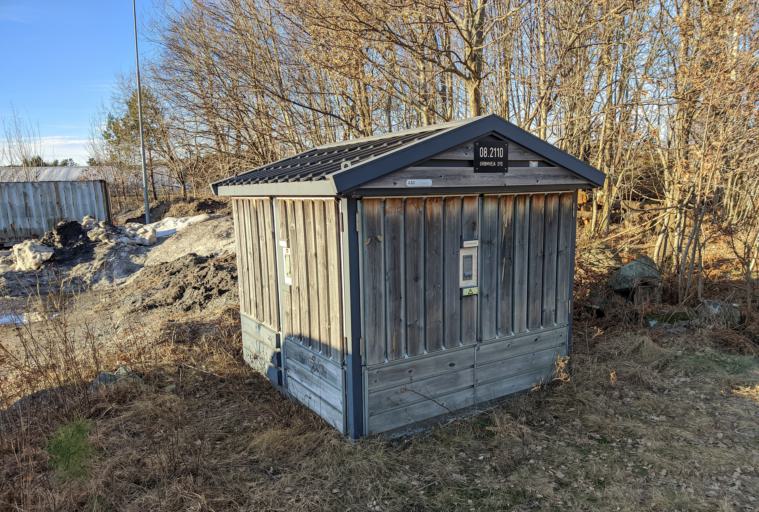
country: NO
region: Aust-Agder
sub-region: Grimstad
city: Grimstad
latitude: 58.3403
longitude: 8.5756
